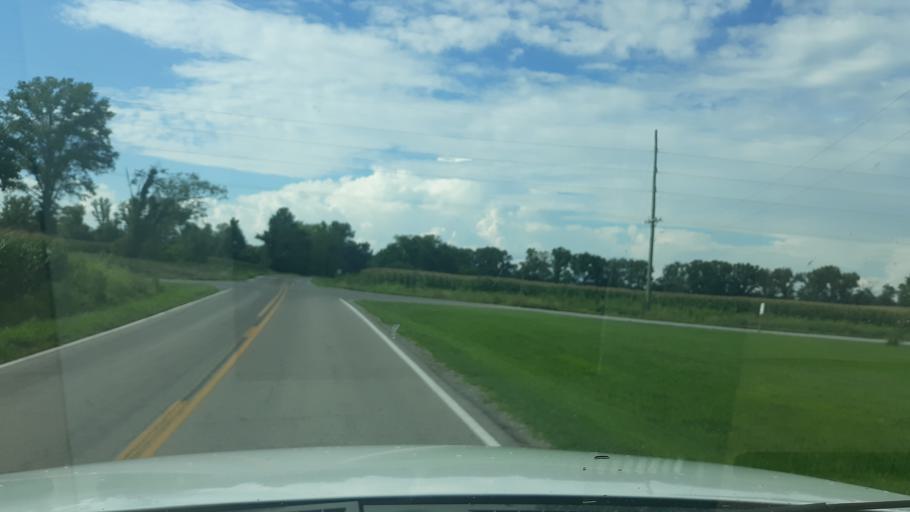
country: US
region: Illinois
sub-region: Saline County
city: Eldorado
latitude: 37.8624
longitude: -88.5306
